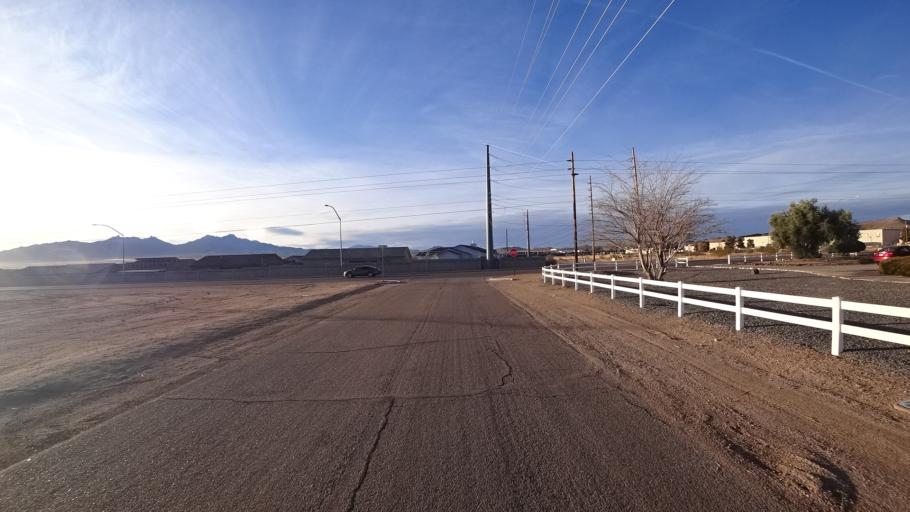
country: US
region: Arizona
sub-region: Mohave County
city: New Kingman-Butler
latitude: 35.2398
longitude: -114.0334
